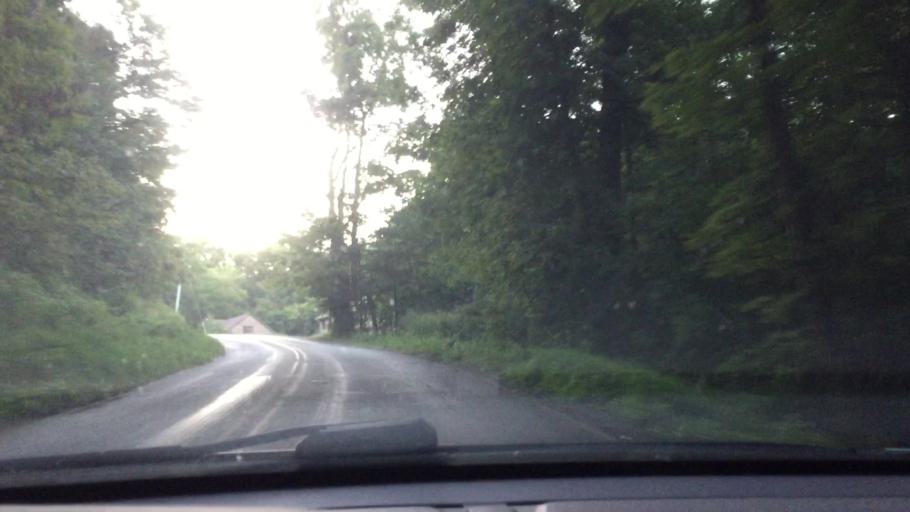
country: US
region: Pennsylvania
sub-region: Washington County
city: Thompsonville
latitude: 40.2689
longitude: -80.1444
